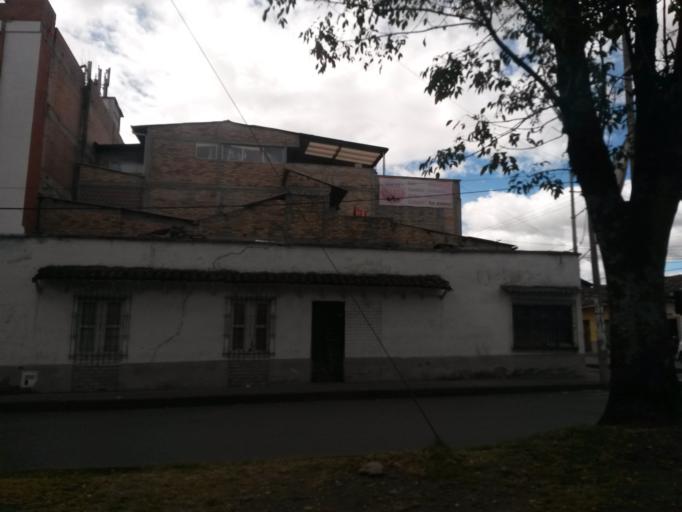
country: CO
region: Cauca
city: Popayan
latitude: 2.4353
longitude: -76.6115
